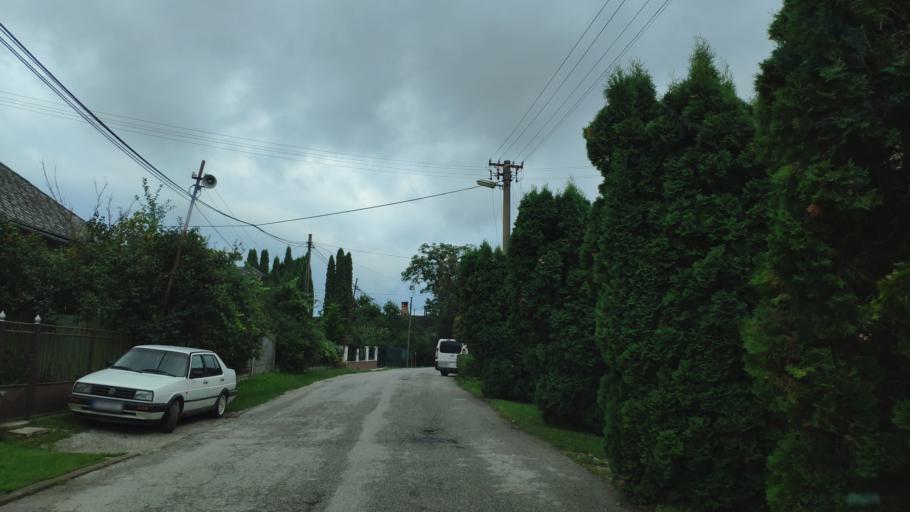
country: SK
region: Kosicky
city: Moldava nad Bodvou
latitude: 48.5818
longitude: 20.8880
